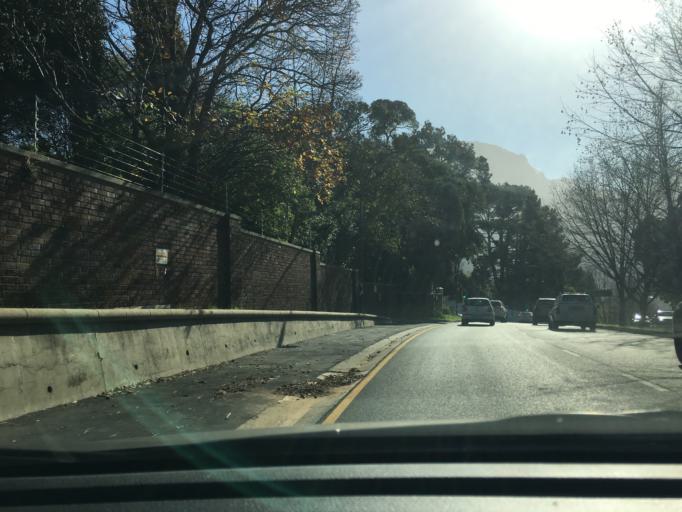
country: ZA
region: Western Cape
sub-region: City of Cape Town
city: Newlands
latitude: -33.9924
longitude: 18.4548
